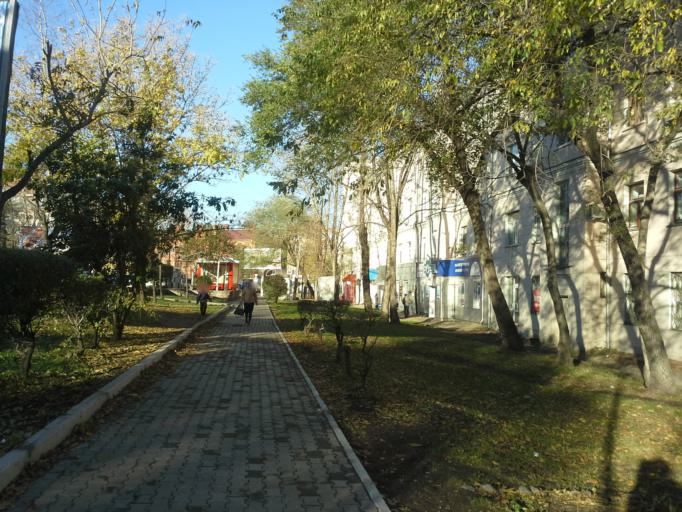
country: RU
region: Khabarovsk Krai
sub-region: Khabarovskiy Rayon
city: Khabarovsk
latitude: 48.4865
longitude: 135.0621
